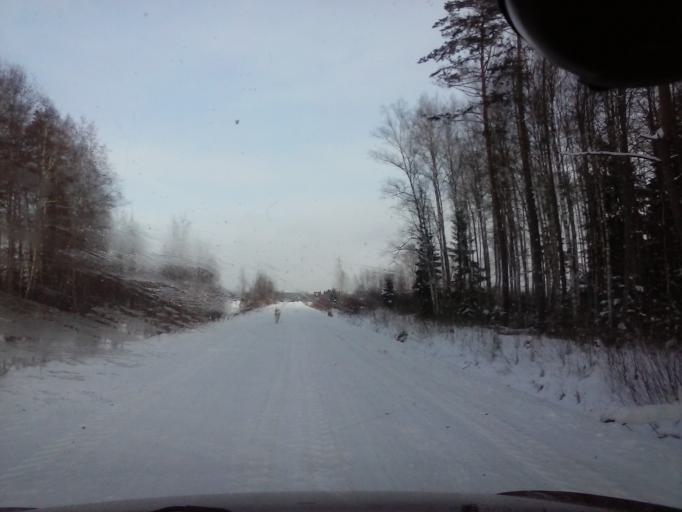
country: EE
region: Paernumaa
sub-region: Paikuse vald
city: Paikuse
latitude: 58.2019
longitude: 24.7218
